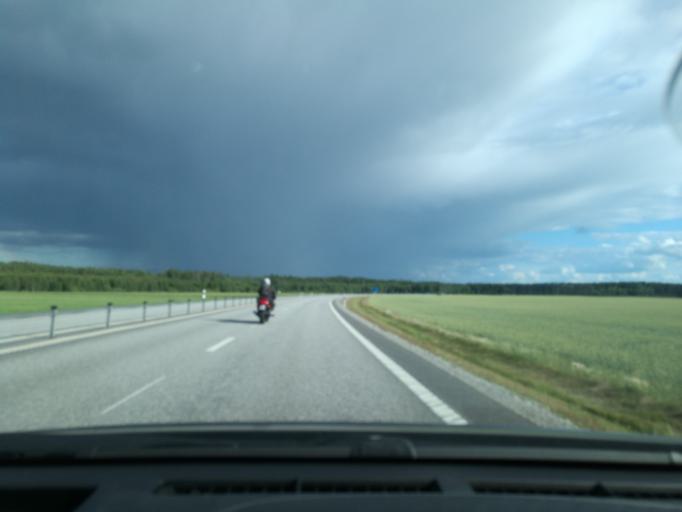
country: SE
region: Vaestmanland
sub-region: Surahammars Kommun
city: Ramnas
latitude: 59.7536
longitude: 16.2217
